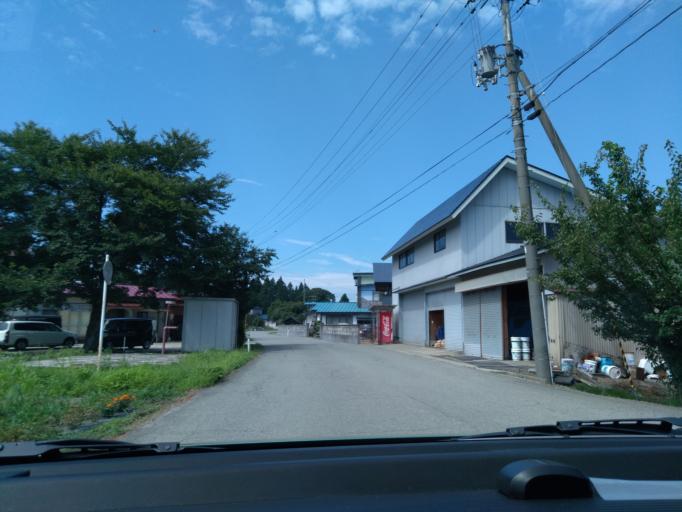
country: JP
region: Akita
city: Kakunodatemachi
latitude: 39.6100
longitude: 140.5944
